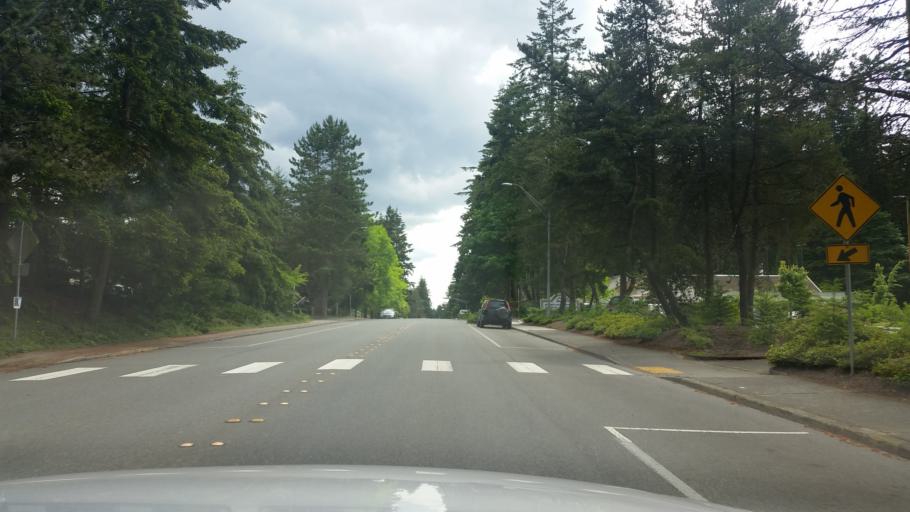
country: US
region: Washington
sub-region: Snohomish County
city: Mountlake Terrace
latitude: 47.7882
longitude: -122.3112
